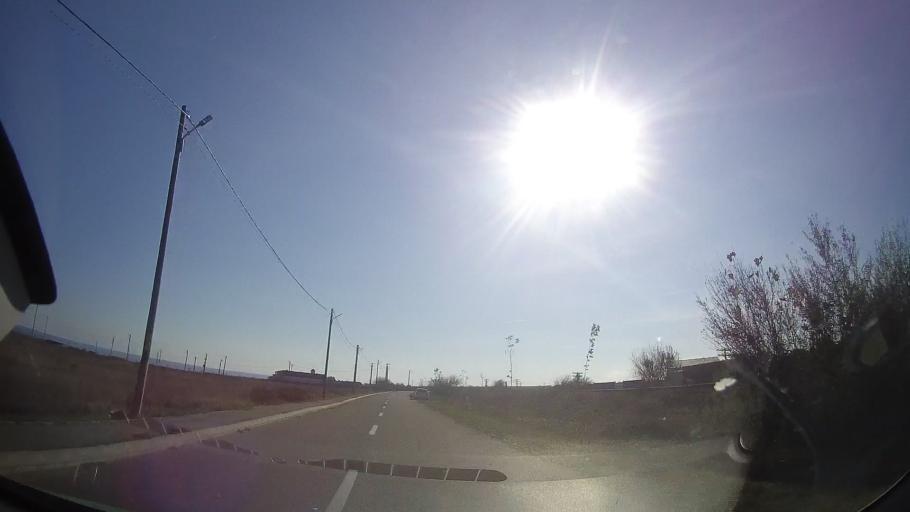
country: RO
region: Constanta
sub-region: Comuna Costinesti
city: Schitu
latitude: 43.9271
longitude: 28.6324
